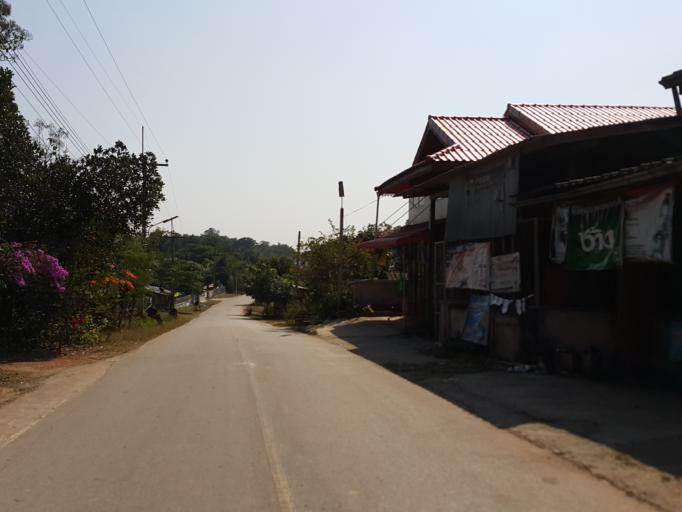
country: TH
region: Lampang
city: Wang Nuea
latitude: 19.0395
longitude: 99.6240
